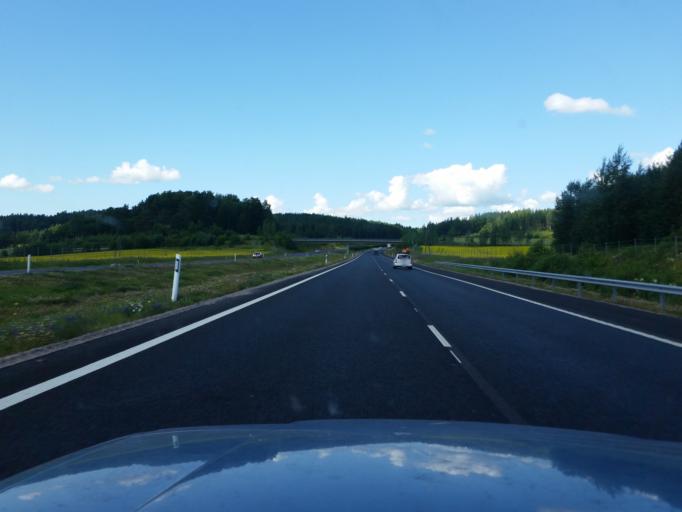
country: FI
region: Varsinais-Suomi
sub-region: Salo
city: Muurla
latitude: 60.3898
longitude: 23.2857
